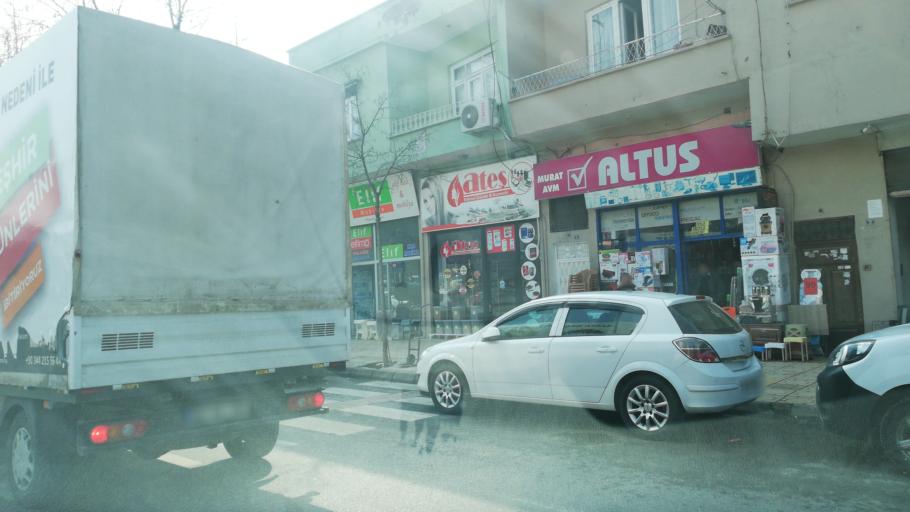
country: TR
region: Kahramanmaras
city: Kahramanmaras
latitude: 37.5786
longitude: 36.9325
